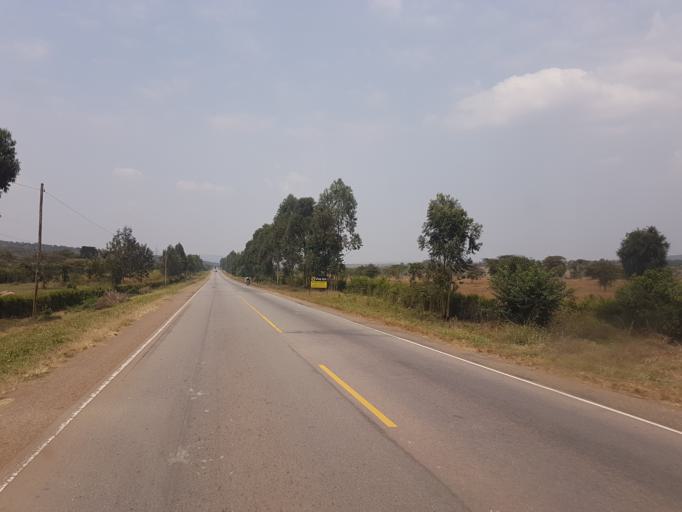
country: UG
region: Western Region
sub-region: Mbarara District
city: Mbarara
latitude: -0.5107
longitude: 30.7783
